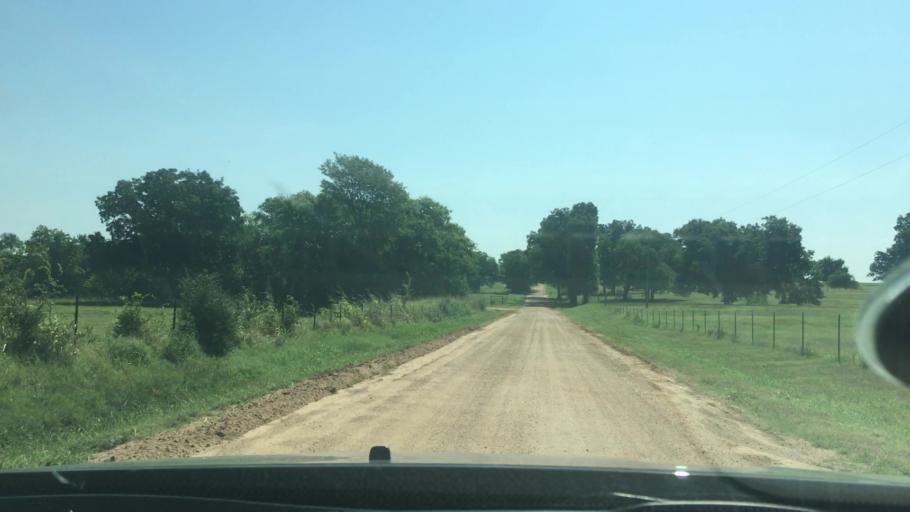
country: US
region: Oklahoma
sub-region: Johnston County
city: Tishomingo
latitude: 34.3104
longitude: -96.6115
